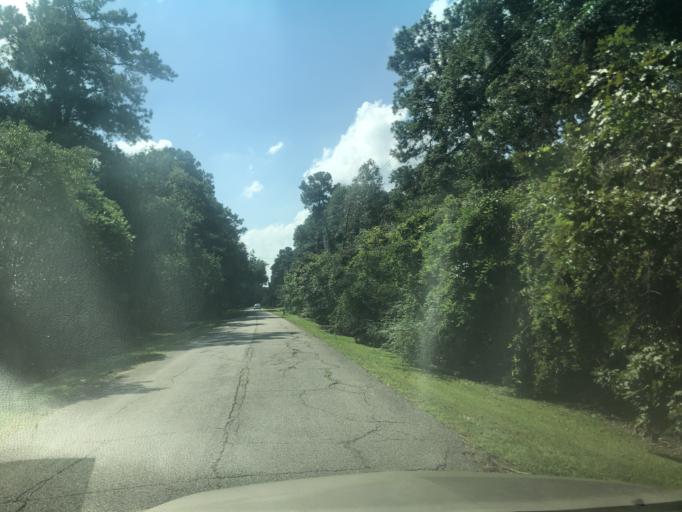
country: US
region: Texas
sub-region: Harris County
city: Bunker Hill Village
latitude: 29.7467
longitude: -95.5460
